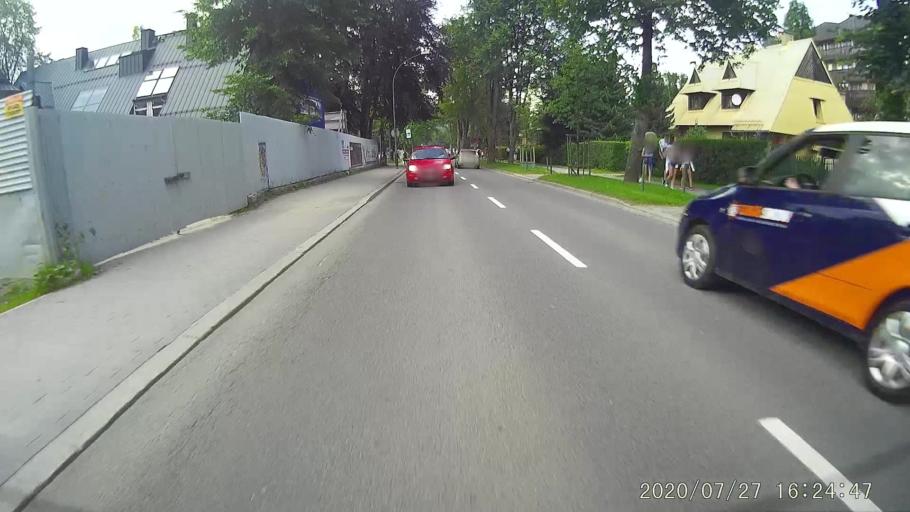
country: PL
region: Lesser Poland Voivodeship
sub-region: Powiat tatrzanski
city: Zakopane
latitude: 49.2978
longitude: 19.9628
